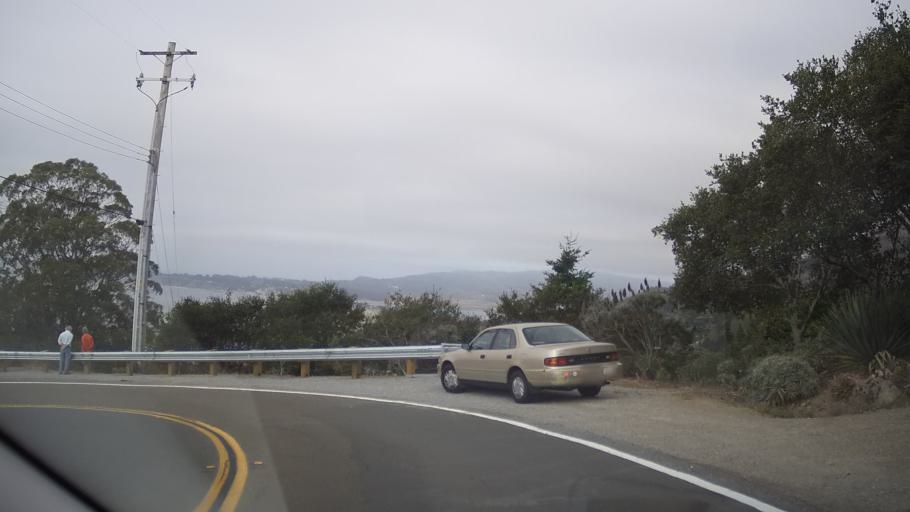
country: US
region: California
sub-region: Marin County
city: Bolinas
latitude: 37.8958
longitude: -122.6297
